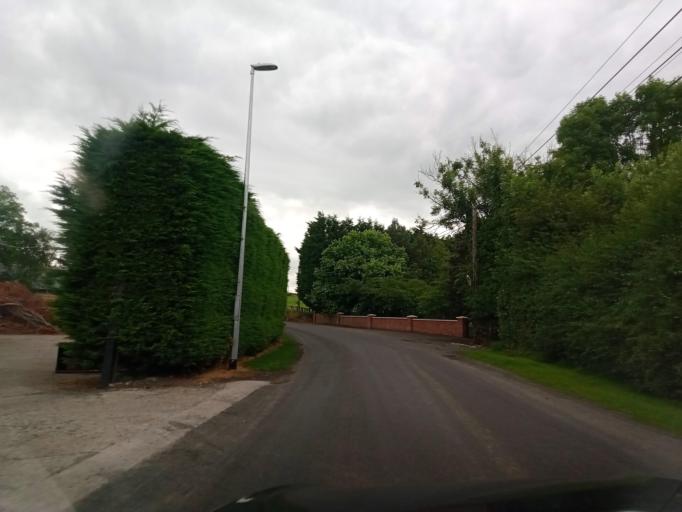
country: IE
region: Leinster
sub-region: Kilkenny
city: Castlecomer
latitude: 52.8931
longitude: -7.1527
